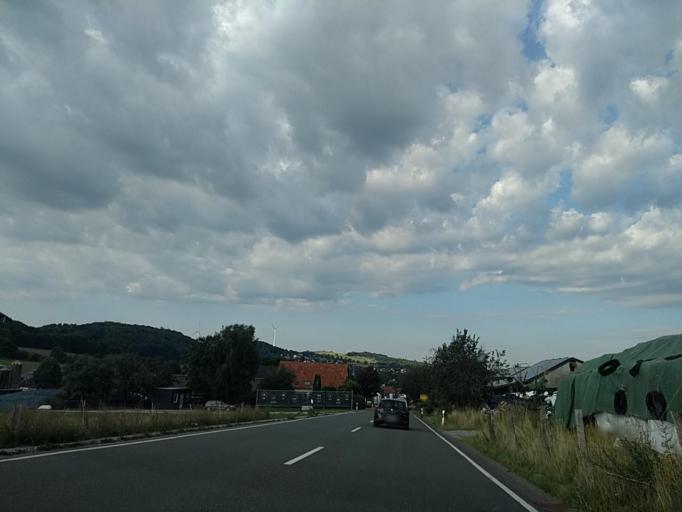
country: DE
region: North Rhine-Westphalia
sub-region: Regierungsbezirk Detmold
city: Wunnenberg
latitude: 51.4630
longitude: 8.6347
